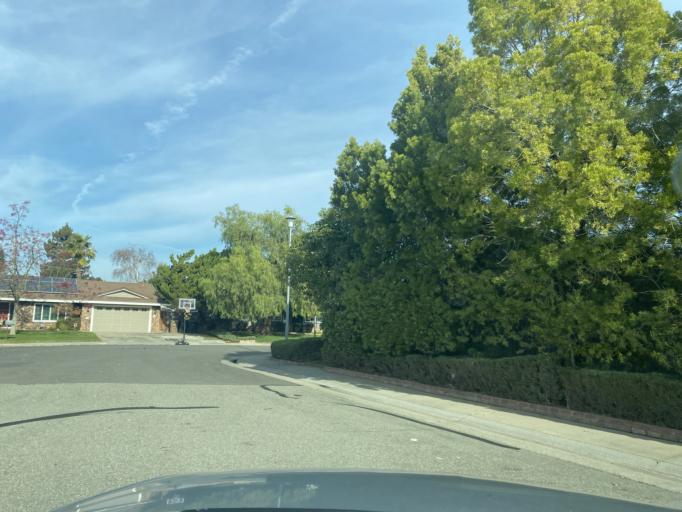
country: US
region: California
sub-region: Sacramento County
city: Elk Grove
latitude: 38.4048
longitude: -121.3806
